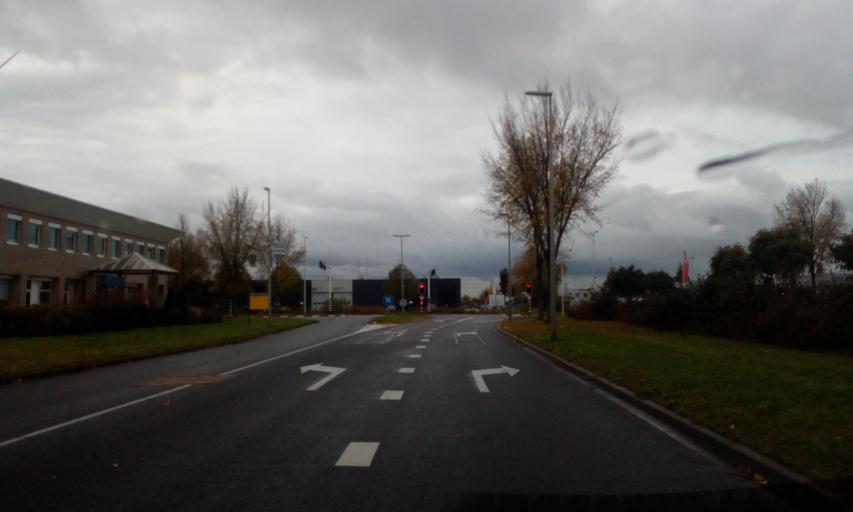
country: NL
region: South Holland
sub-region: Gemeente Zoetermeer
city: Zoetermeer
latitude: 52.0374
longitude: 4.5068
